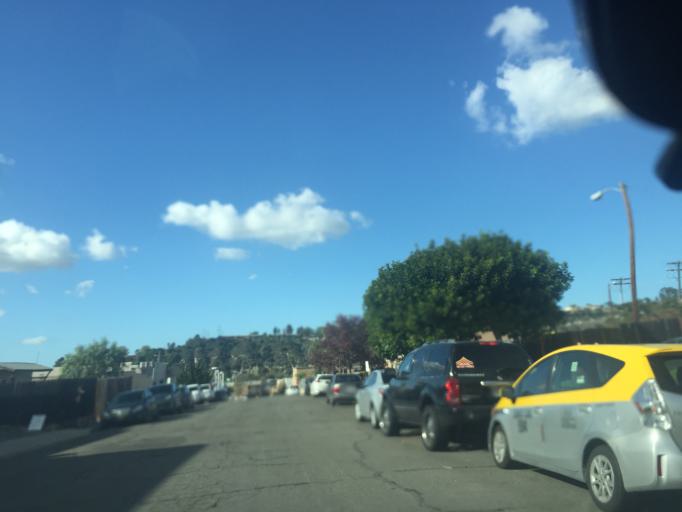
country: US
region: California
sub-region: San Diego County
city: La Mesa
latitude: 32.7893
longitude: -117.0965
